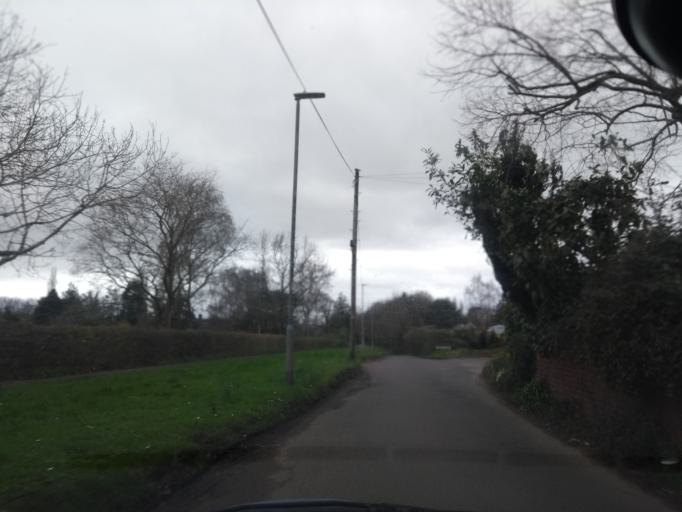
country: GB
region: England
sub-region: Somerset
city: Taunton
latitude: 51.0362
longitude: -3.1039
